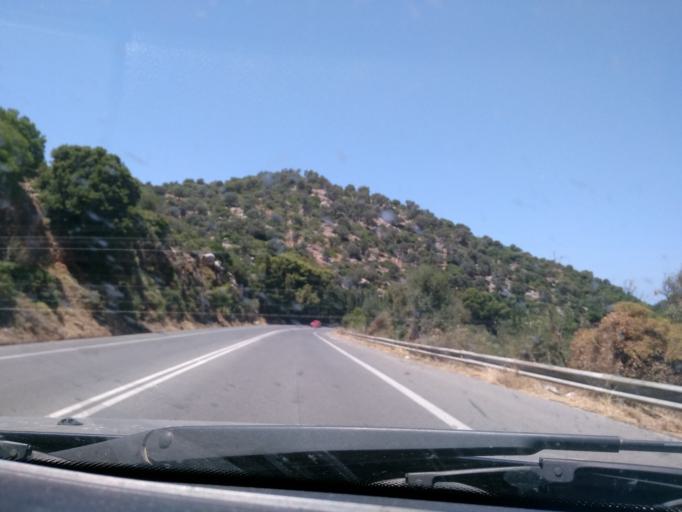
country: GR
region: Crete
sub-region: Nomos Rethymnis
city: Anogeia
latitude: 35.3920
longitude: 24.8801
